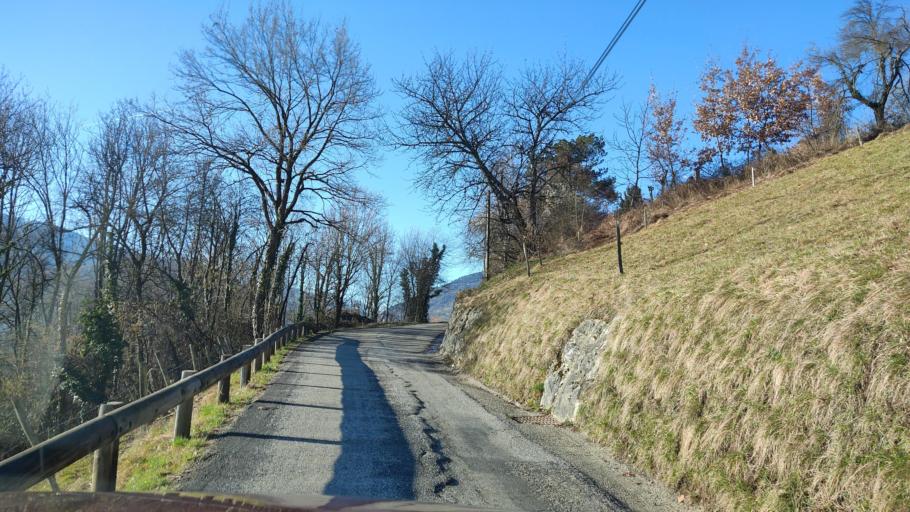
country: FR
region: Rhone-Alpes
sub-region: Departement de la Savoie
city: La Rochette
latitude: 45.4639
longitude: 6.1082
